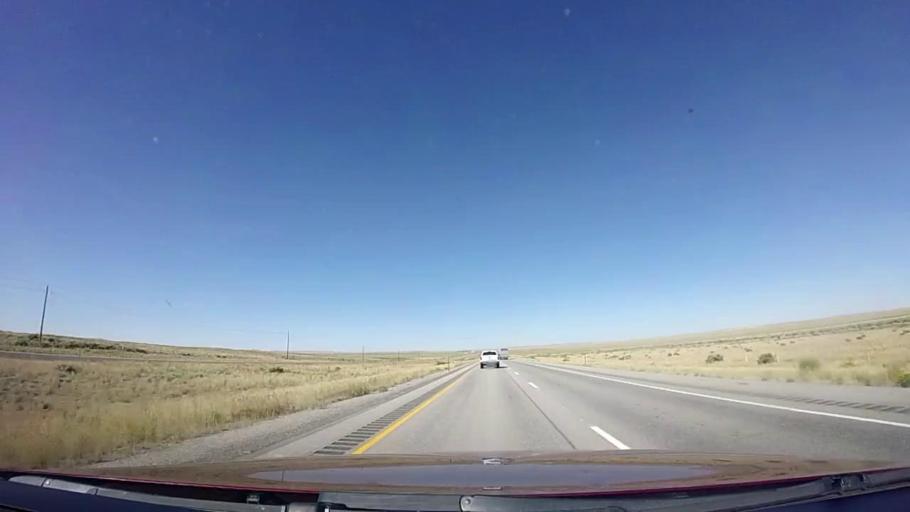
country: US
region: Wyoming
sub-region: Carbon County
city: Rawlins
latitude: 41.7796
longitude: -107.4375
